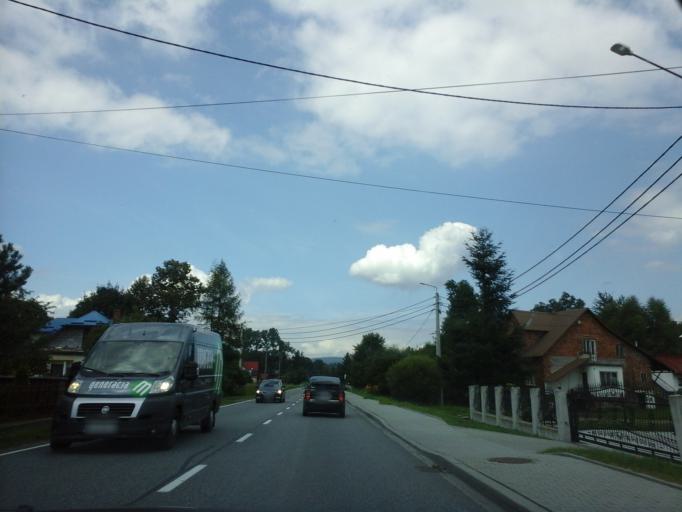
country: PL
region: Lesser Poland Voivodeship
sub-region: Powiat suski
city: Juszczyn
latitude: 49.7015
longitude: 19.6999
